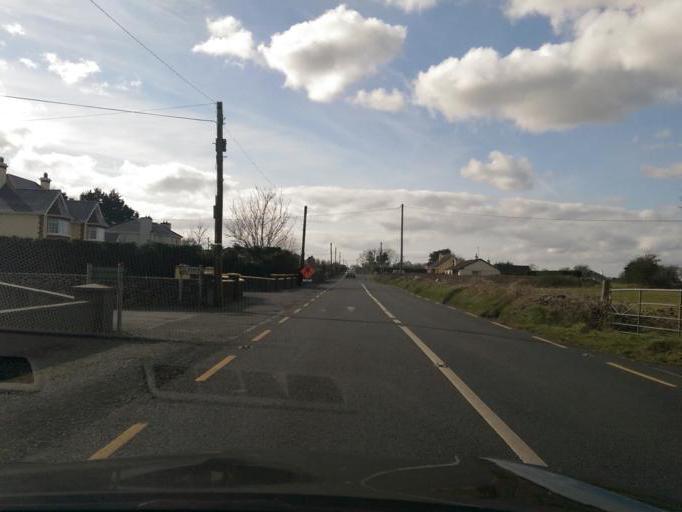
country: IE
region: Connaught
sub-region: County Galway
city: Oranmore
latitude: 53.3137
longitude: -8.8816
